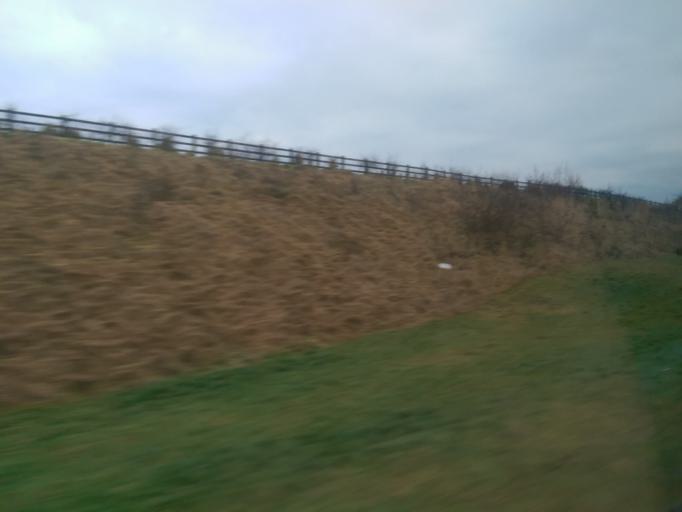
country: IE
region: Connaught
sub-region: County Galway
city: Loughrea
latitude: 53.2816
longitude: -8.4213
